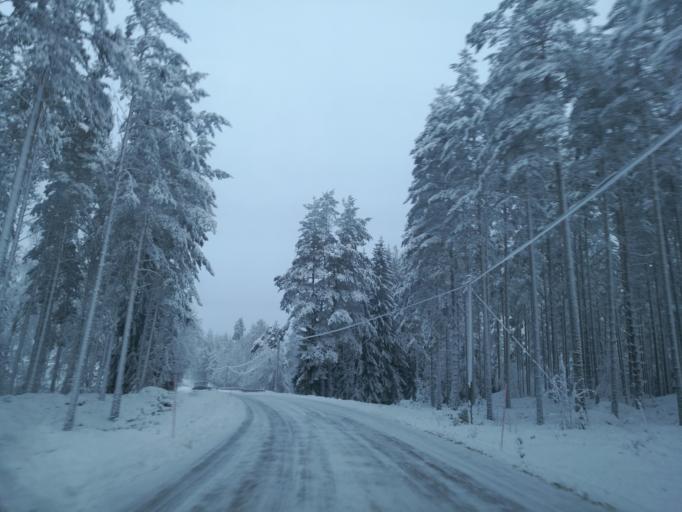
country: NO
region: Hedmark
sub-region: Grue
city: Kirkenaer
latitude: 60.5009
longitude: 12.5596
